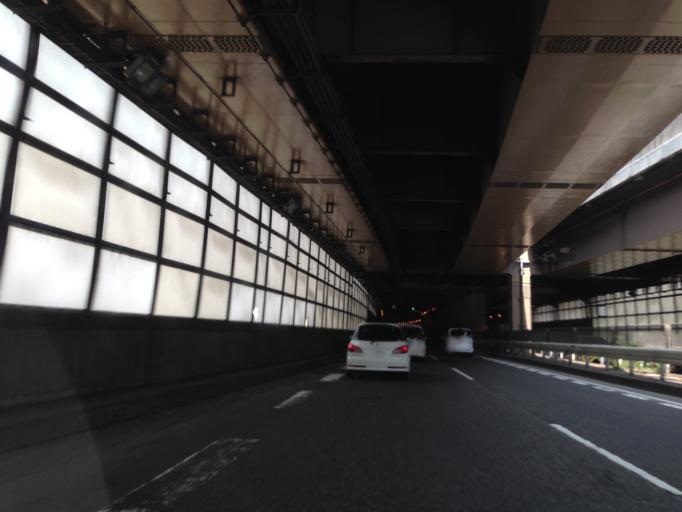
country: JP
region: Miyagi
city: Sendai
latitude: 38.2613
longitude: 140.8599
